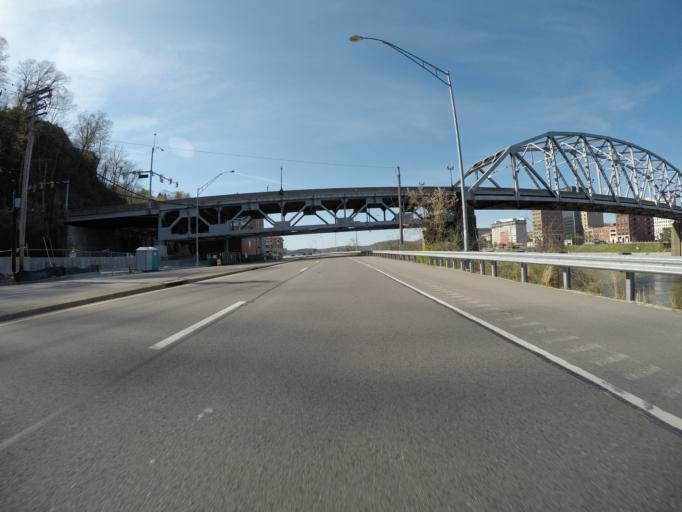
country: US
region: West Virginia
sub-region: Kanawha County
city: Charleston
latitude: 38.3458
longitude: -81.6372
